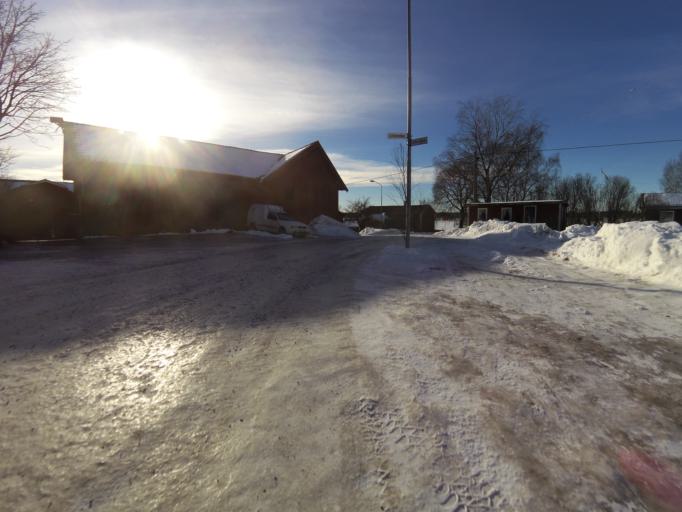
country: SE
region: Gaevleborg
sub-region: Gavle Kommun
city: Valbo
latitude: 60.6520
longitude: 17.0670
